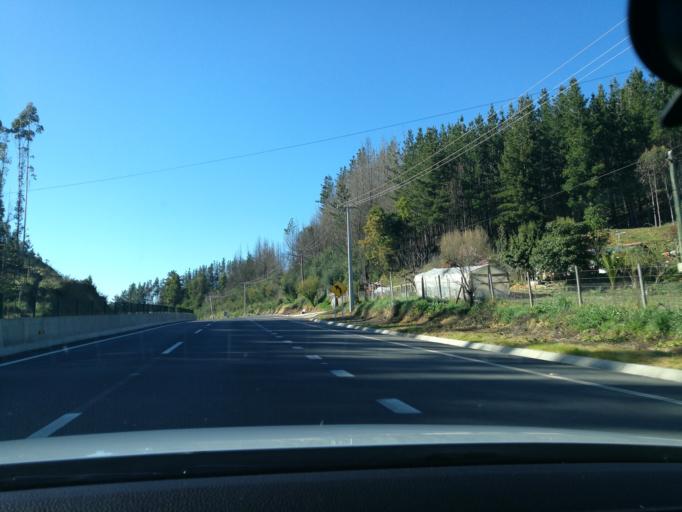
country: CL
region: Biobio
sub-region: Provincia de Concepcion
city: Chiguayante
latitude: -36.8540
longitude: -72.8967
